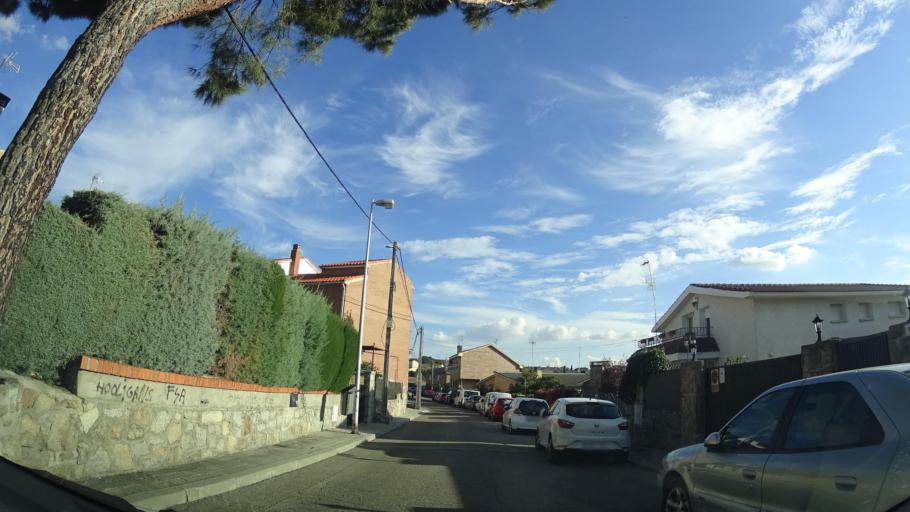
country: ES
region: Madrid
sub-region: Provincia de Madrid
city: Colmenarejo
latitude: 40.5620
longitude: -4.0196
